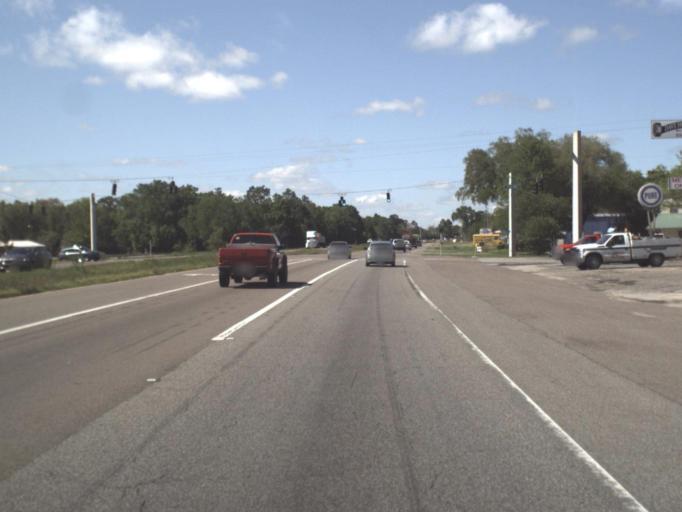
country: US
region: Florida
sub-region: Escambia County
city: Ensley
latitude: 30.5399
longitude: -87.2802
